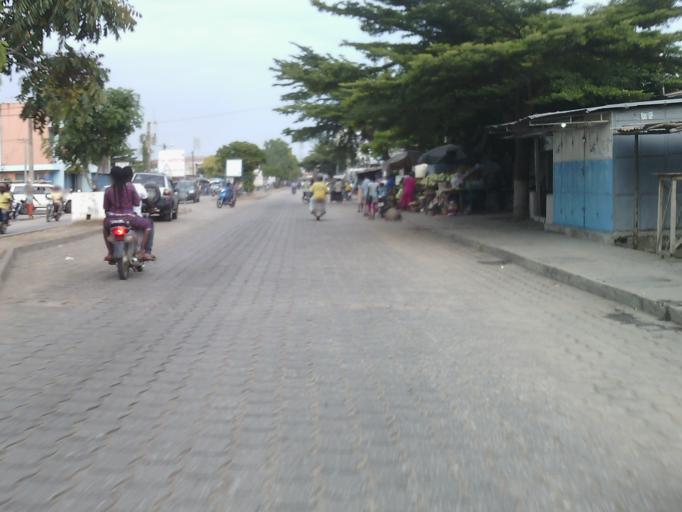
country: BJ
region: Littoral
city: Cotonou
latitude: 6.3898
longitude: 2.3720
